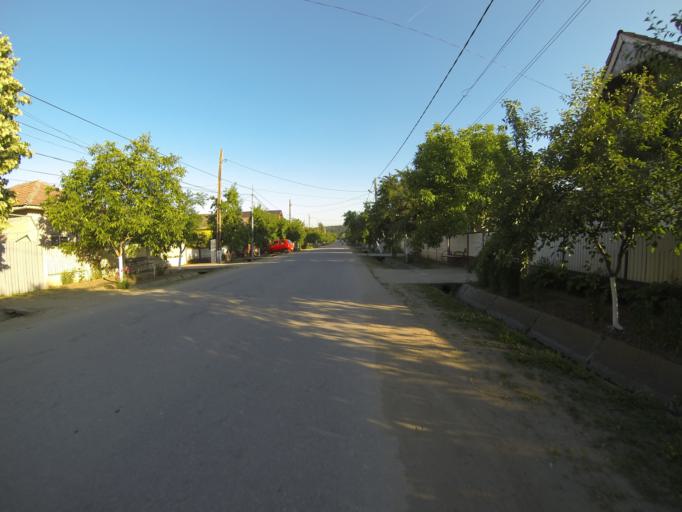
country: RO
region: Dolj
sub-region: Comuna Tuglui
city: Tuglui
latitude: 44.1820
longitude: 23.8145
